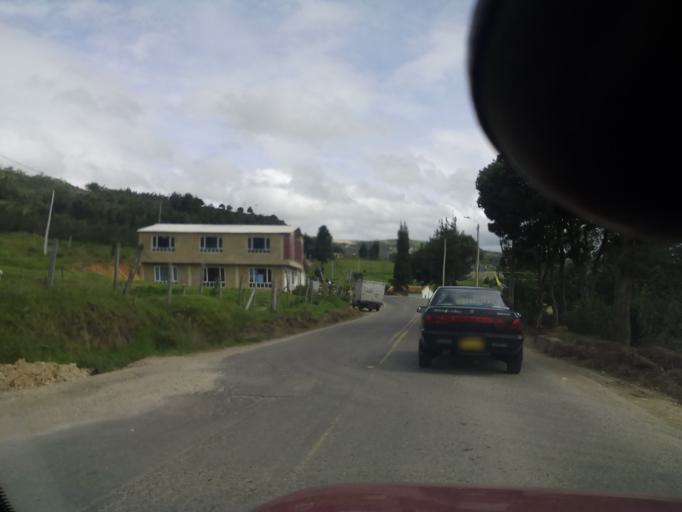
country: CO
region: Boyaca
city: Combita
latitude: 5.6278
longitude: -73.3144
